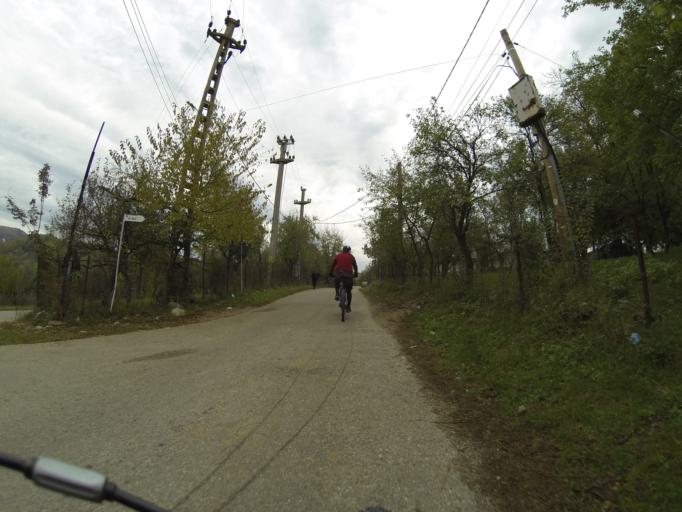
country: RO
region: Gorj
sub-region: Comuna Tismana
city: Sohodol
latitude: 45.0477
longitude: 22.8963
